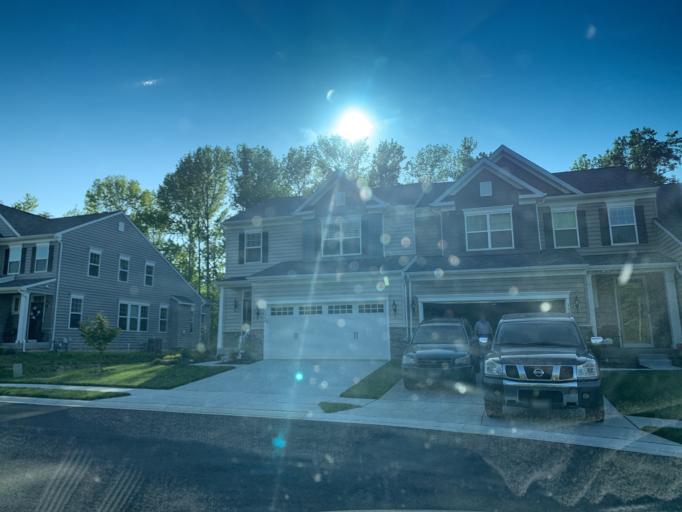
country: US
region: Maryland
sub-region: Harford County
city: Riverside
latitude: 39.4610
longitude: -76.2680
